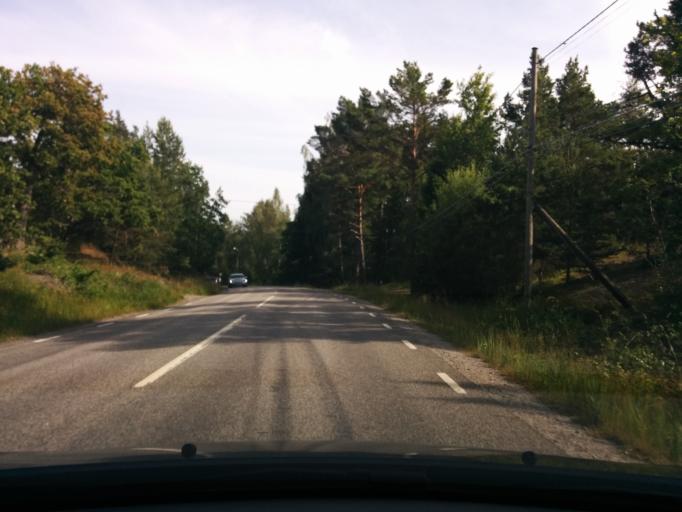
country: SE
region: Stockholm
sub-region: Varmdo Kommun
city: Holo
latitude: 59.3233
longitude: 18.7232
